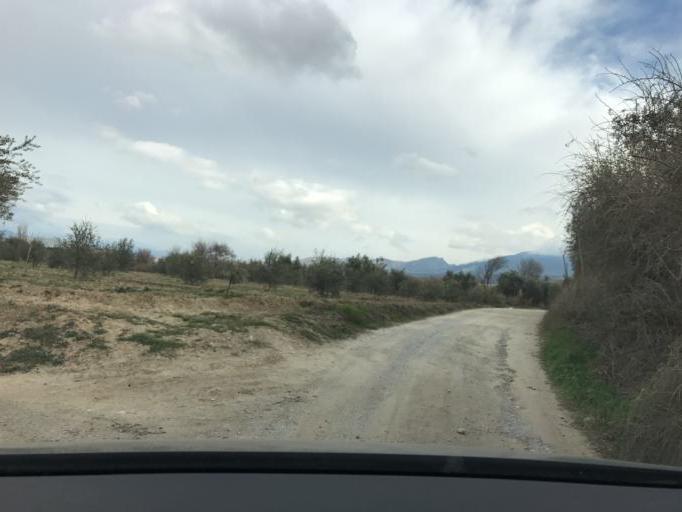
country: ES
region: Andalusia
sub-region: Provincia de Granada
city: Otura
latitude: 37.0977
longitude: -3.6313
